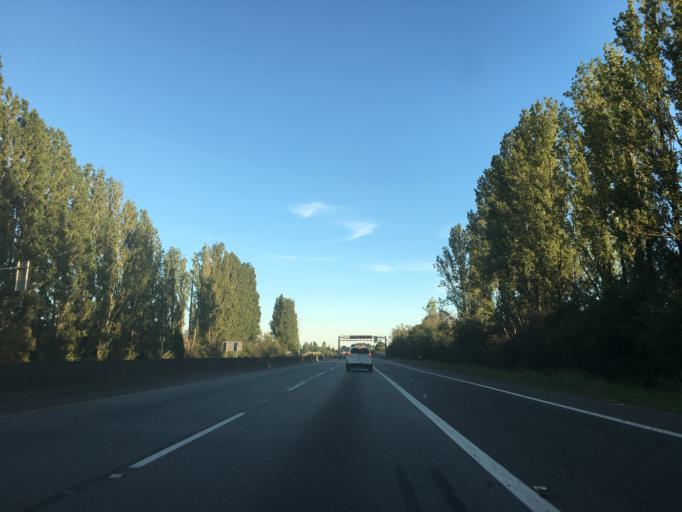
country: CA
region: British Columbia
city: Ladner
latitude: 49.1438
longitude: -123.0869
